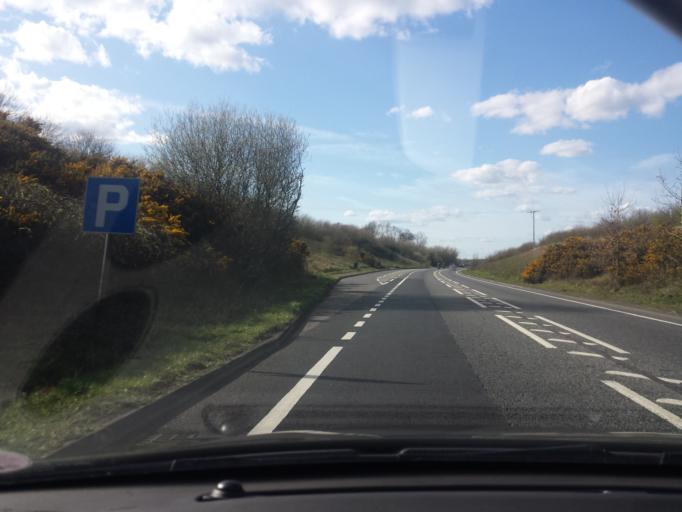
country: GB
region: England
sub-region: Essex
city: Little Clacton
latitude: 51.8462
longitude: 1.1062
